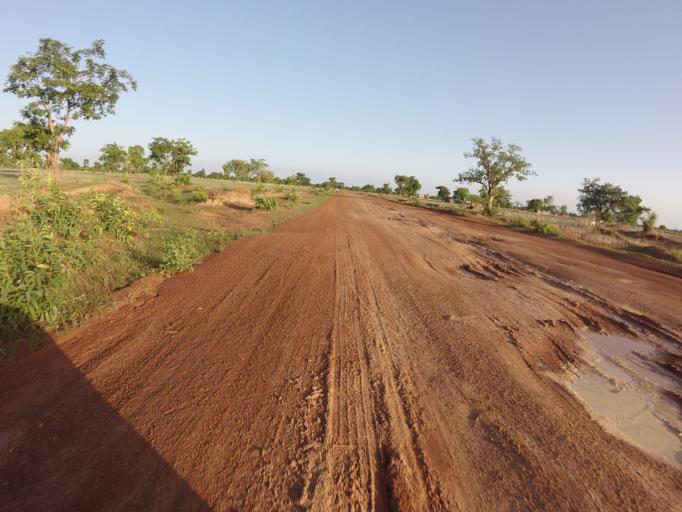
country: TG
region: Savanes
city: Sansanne-Mango
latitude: 10.2924
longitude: -0.0873
